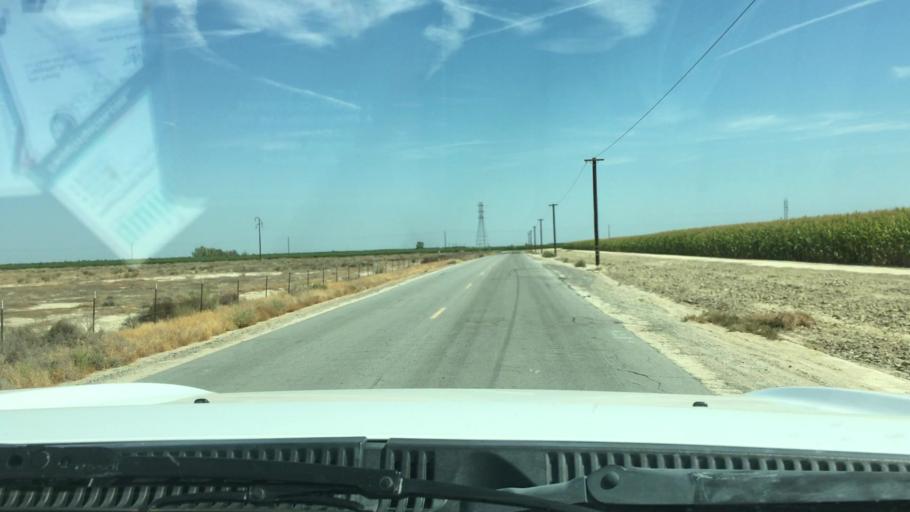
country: US
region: California
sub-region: Kern County
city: Buttonwillow
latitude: 35.4380
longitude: -119.3760
